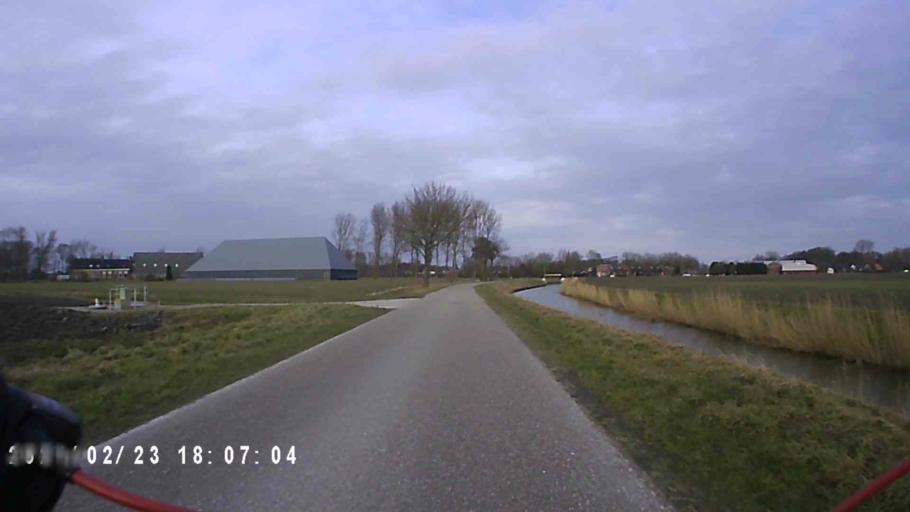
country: NL
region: Groningen
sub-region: Gemeente Bedum
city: Bedum
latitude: 53.3977
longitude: 6.6041
